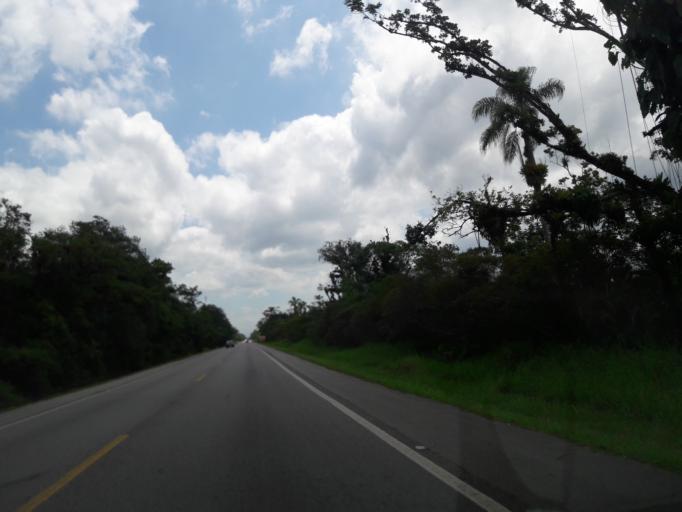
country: BR
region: Parana
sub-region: Pontal Do Parana
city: Pontal do Parana
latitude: -25.6466
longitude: -48.5297
